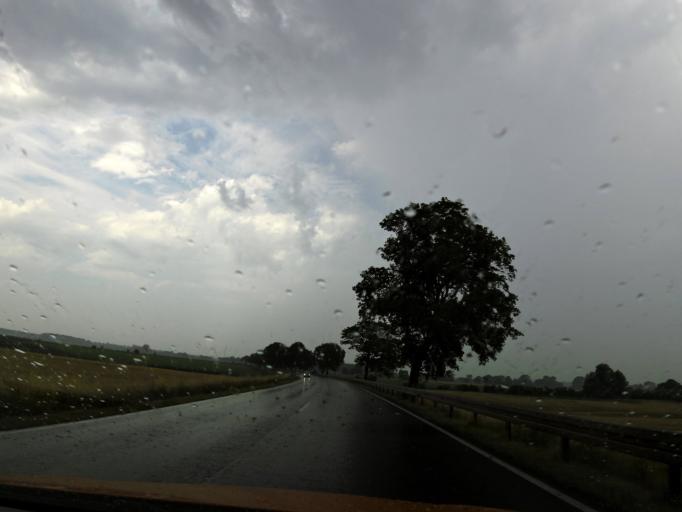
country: DE
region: Brandenburg
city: Pessin
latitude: 52.6527
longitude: 12.6524
